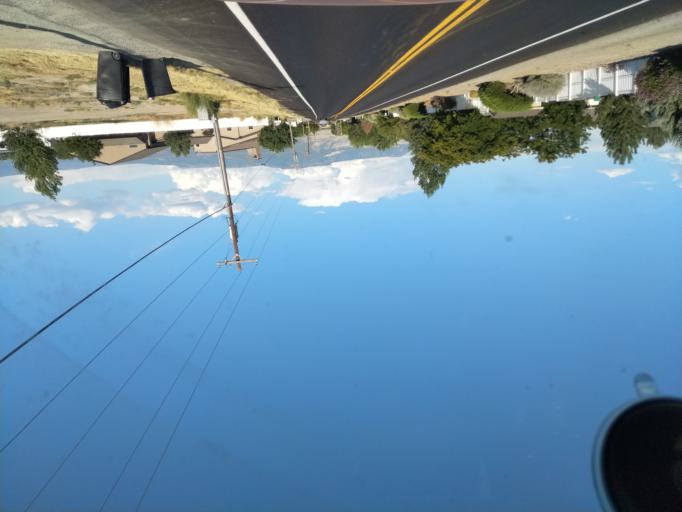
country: US
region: Colorado
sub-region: Mesa County
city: Fruitvale
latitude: 39.0629
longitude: -108.4688
